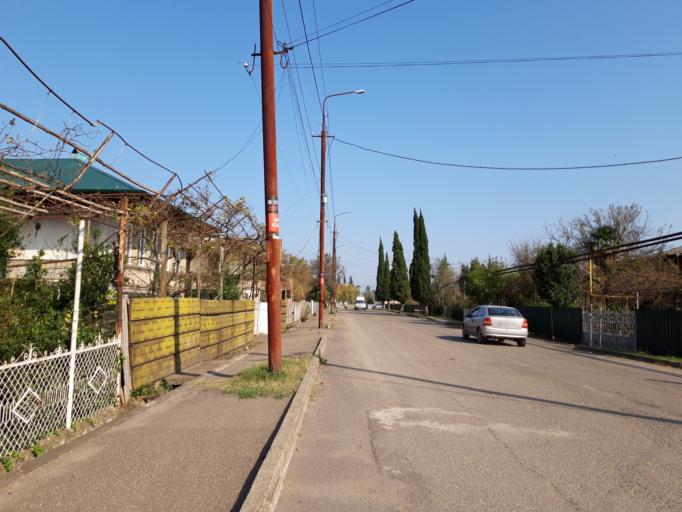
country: GE
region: Imereti
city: Samtredia
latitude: 42.1606
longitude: 42.3268
